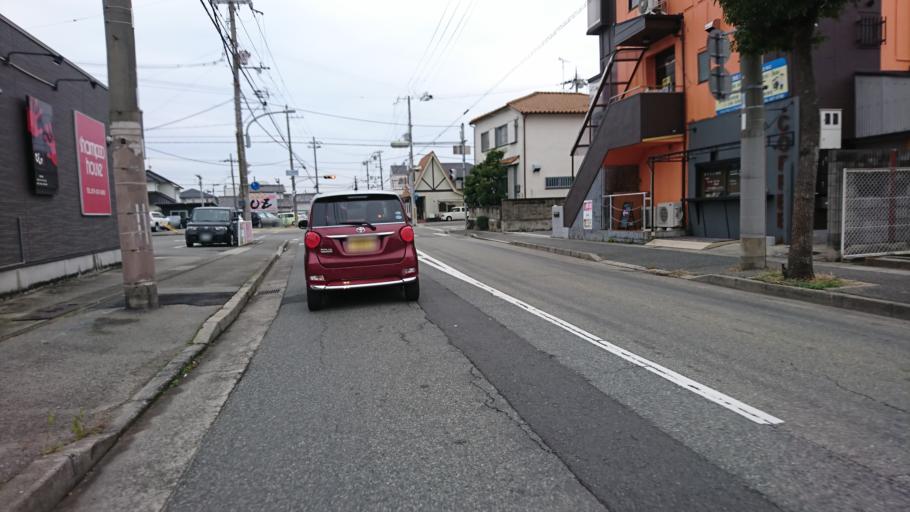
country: JP
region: Hyogo
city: Kakogawacho-honmachi
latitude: 34.7660
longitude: 134.8207
